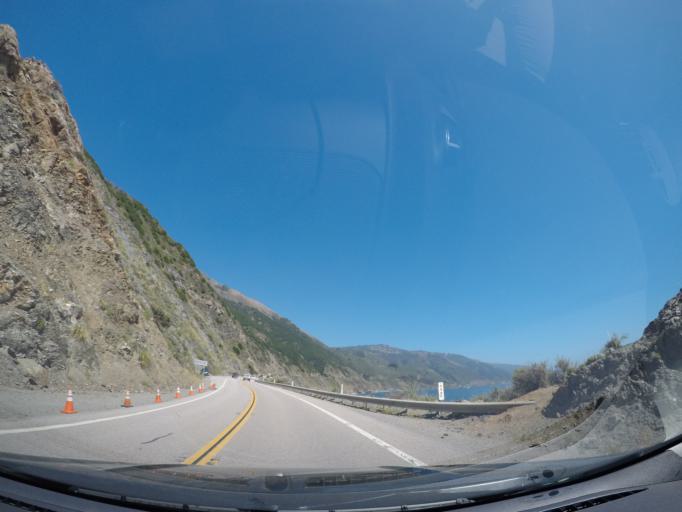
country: US
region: California
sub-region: Monterey County
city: Greenfield
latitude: 36.0085
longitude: -121.5180
